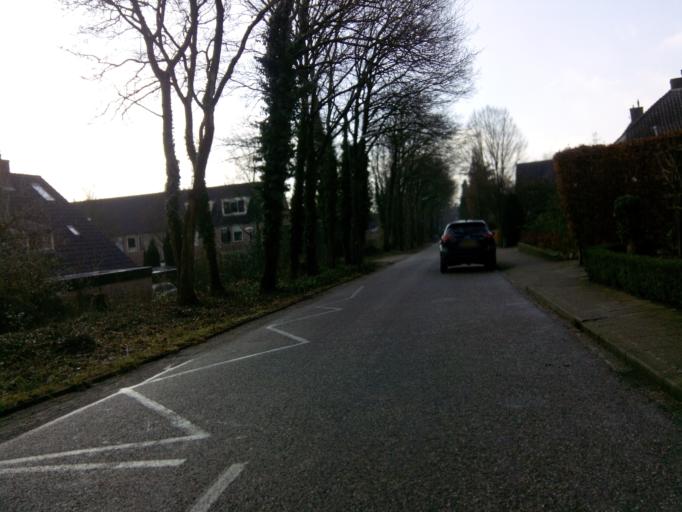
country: NL
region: Utrecht
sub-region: Gemeente Utrechtse Heuvelrug
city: Amerongen
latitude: 52.0051
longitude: 5.4685
